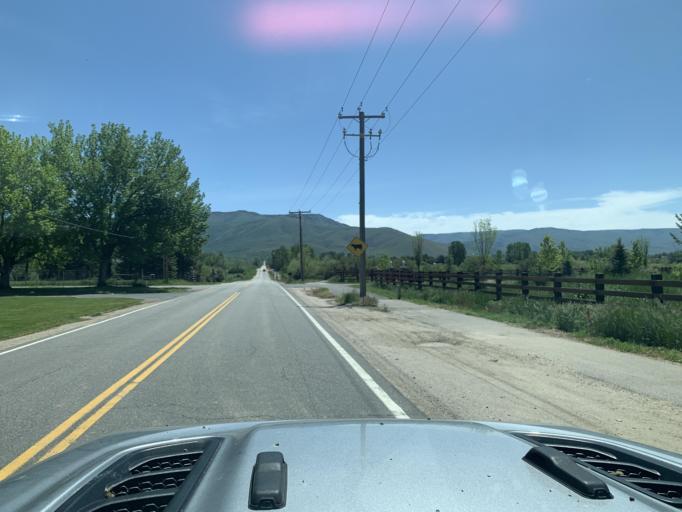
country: US
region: Utah
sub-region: Weber County
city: Wolf Creek
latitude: 41.2932
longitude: -111.7936
